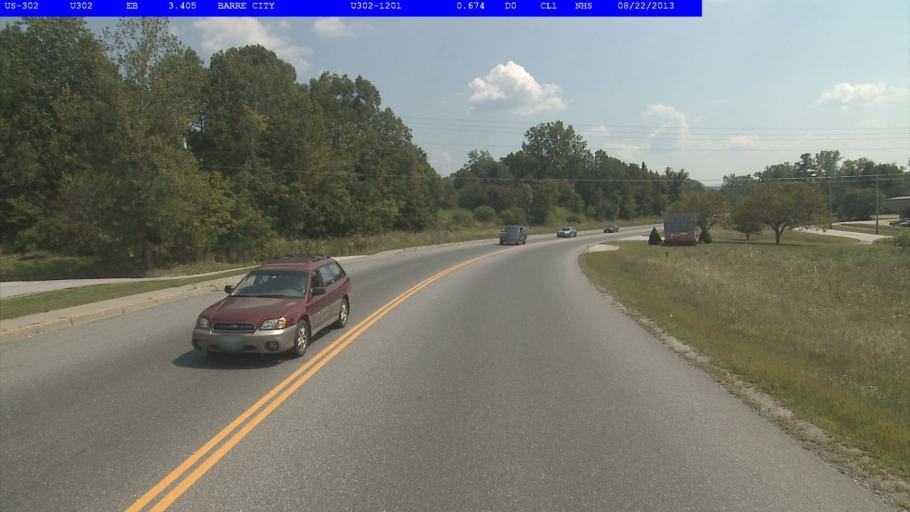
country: US
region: Vermont
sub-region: Washington County
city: Barre
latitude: 44.2129
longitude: -72.5215
